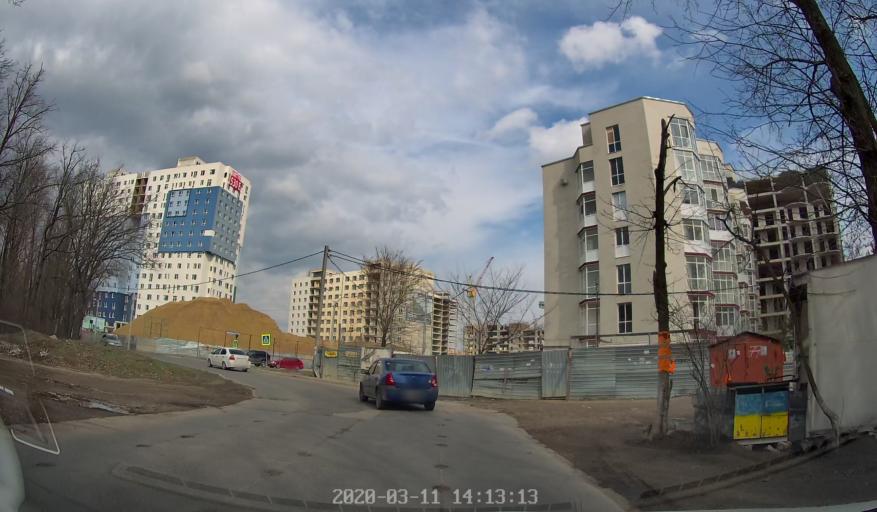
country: MD
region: Chisinau
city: Stauceni
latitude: 47.0566
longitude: 28.8861
